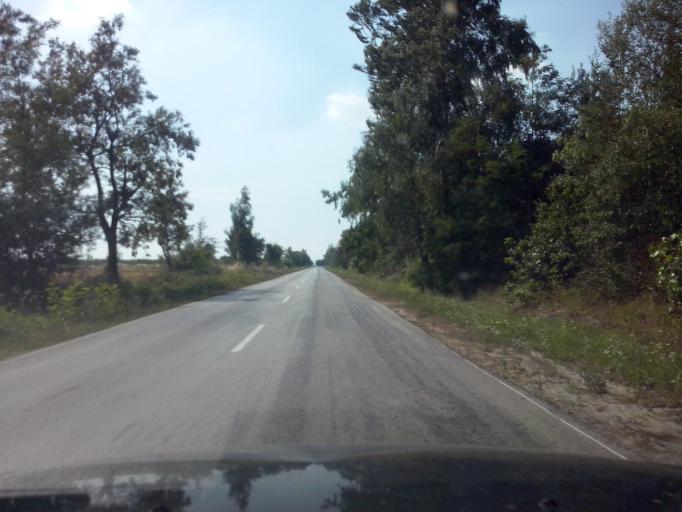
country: PL
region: Swietokrzyskie
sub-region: Powiat staszowski
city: Szydlow
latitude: 50.6186
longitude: 21.0137
